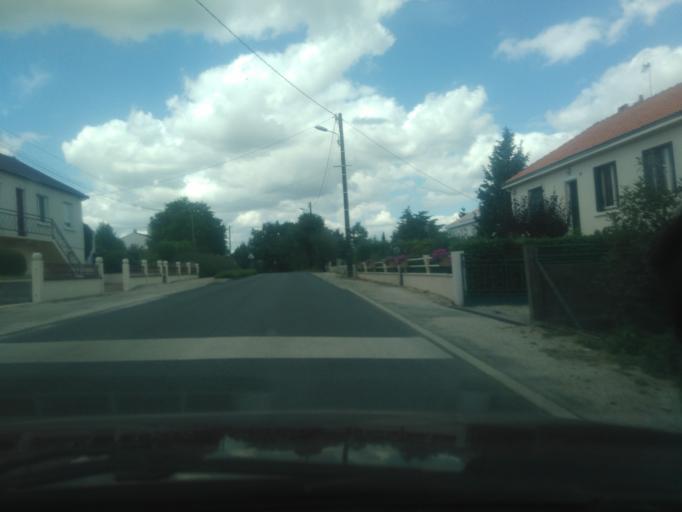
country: FR
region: Pays de la Loire
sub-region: Departement de la Vendee
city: Chauche
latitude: 46.8240
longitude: -1.2674
